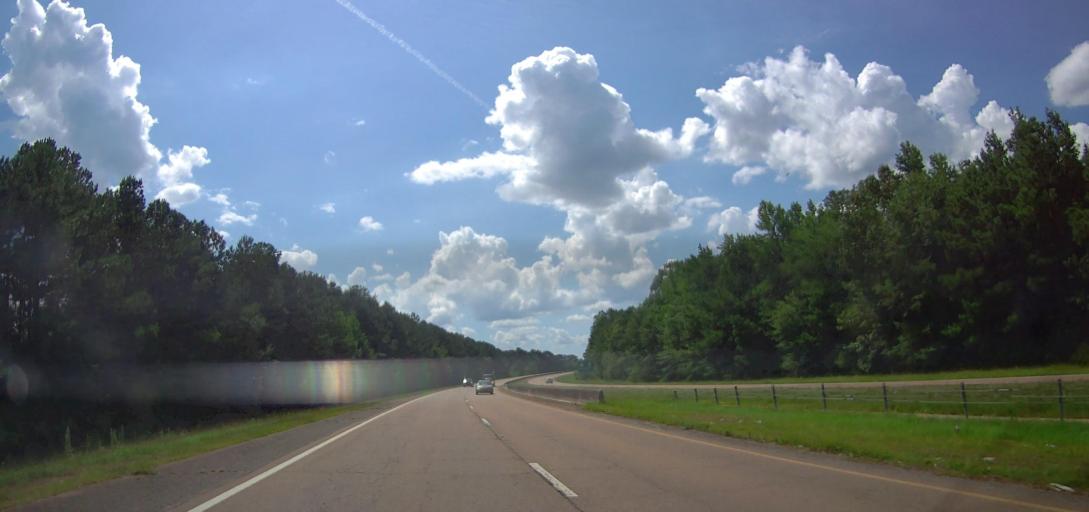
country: US
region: Mississippi
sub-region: Lowndes County
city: New Hope
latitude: 33.5082
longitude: -88.3561
